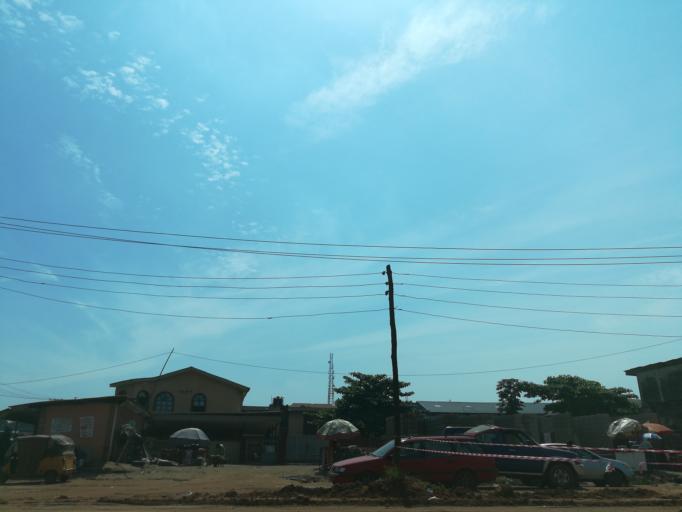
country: NG
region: Lagos
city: Ikorodu
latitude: 6.6538
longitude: 3.4764
